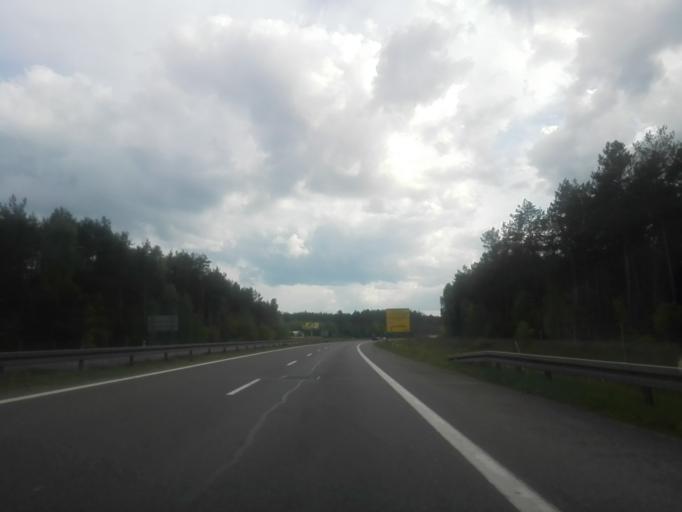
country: PL
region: Masovian Voivodeship
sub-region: Powiat ostrowski
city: Ostrow Mazowiecka
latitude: 52.7923
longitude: 21.8670
